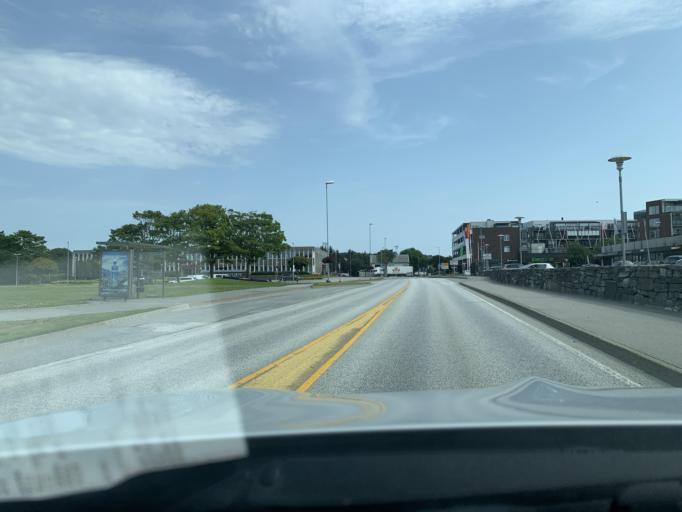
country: NO
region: Rogaland
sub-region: Klepp
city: Kleppe
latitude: 58.7772
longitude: 5.6273
